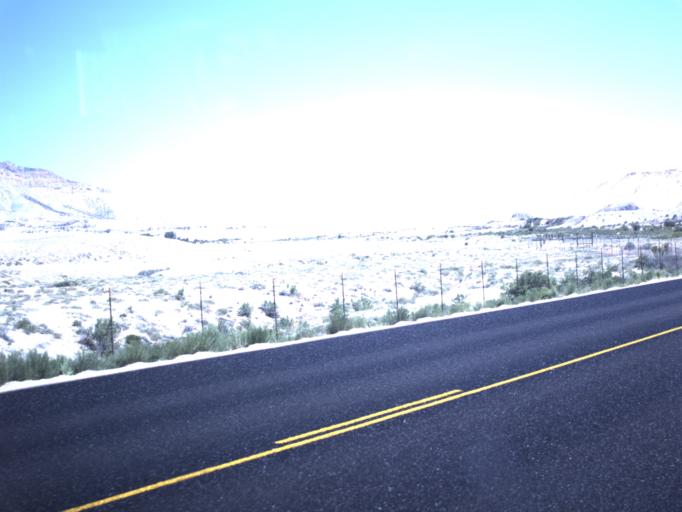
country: US
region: Utah
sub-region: Emery County
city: Ferron
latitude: 38.9617
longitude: -111.1955
